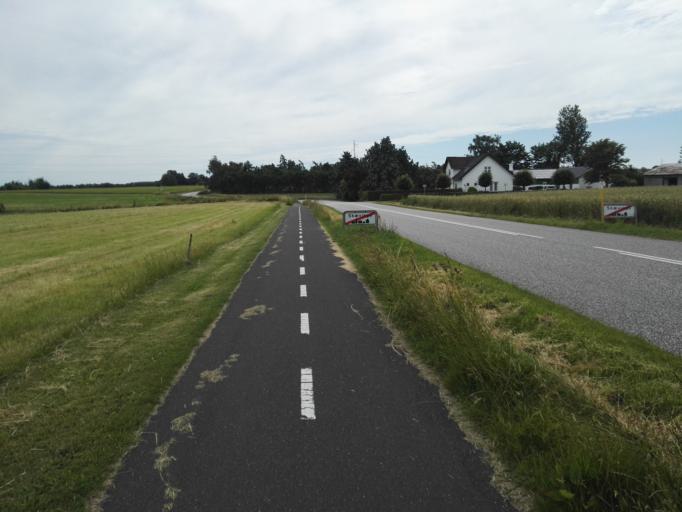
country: DK
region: Capital Region
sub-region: Hillerod Kommune
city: Skaevinge
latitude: 55.9009
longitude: 12.1513
